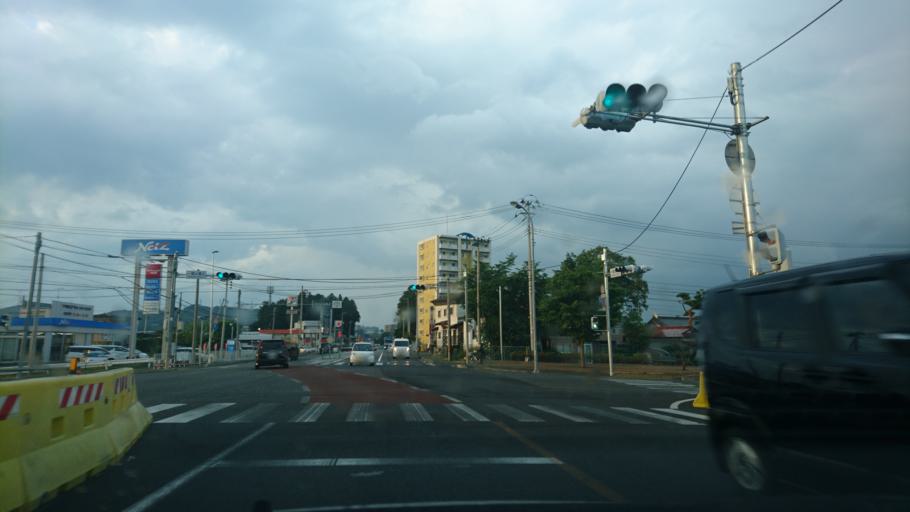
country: JP
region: Iwate
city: Ichinoseki
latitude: 38.9277
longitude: 141.1152
